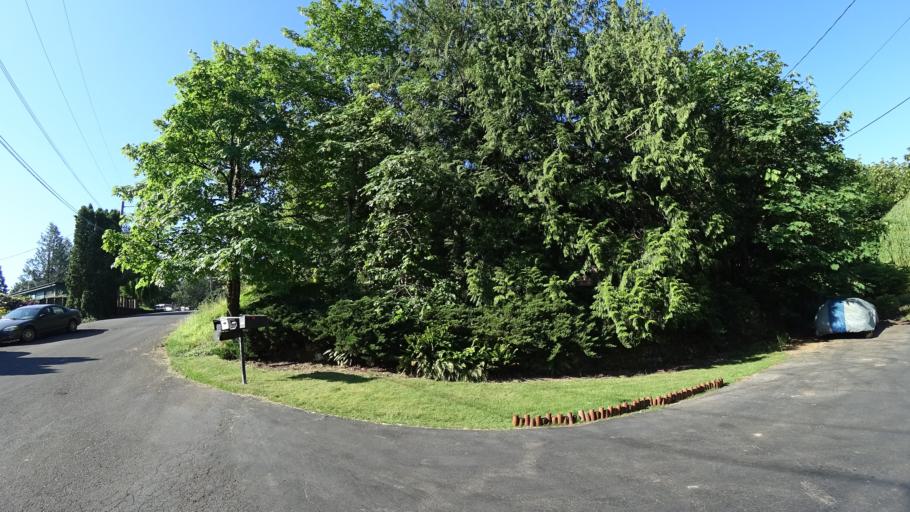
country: US
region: Oregon
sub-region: Clackamas County
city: Happy Valley
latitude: 45.4706
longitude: -122.5415
